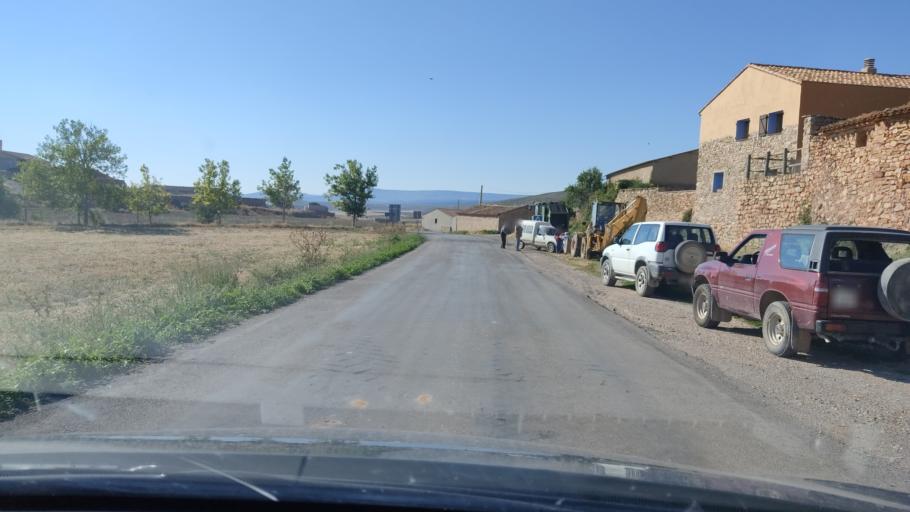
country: ES
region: Aragon
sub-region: Provincia de Teruel
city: Monforte de Moyuela
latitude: 41.0553
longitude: -1.0132
